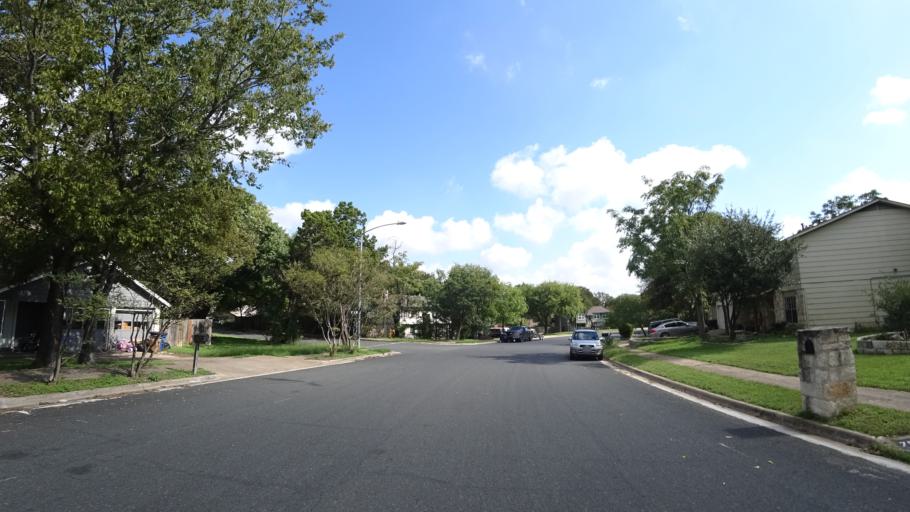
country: US
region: Texas
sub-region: Travis County
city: Shady Hollow
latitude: 30.1990
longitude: -97.8133
